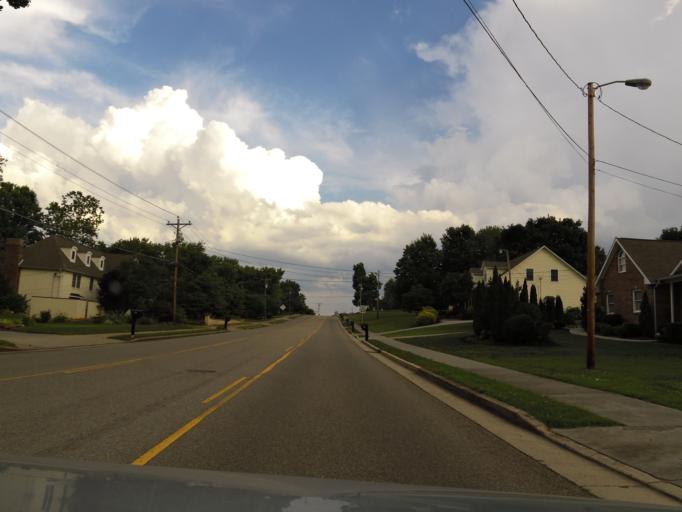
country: US
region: Tennessee
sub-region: Knox County
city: Farragut
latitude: 35.8631
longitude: -84.2020
